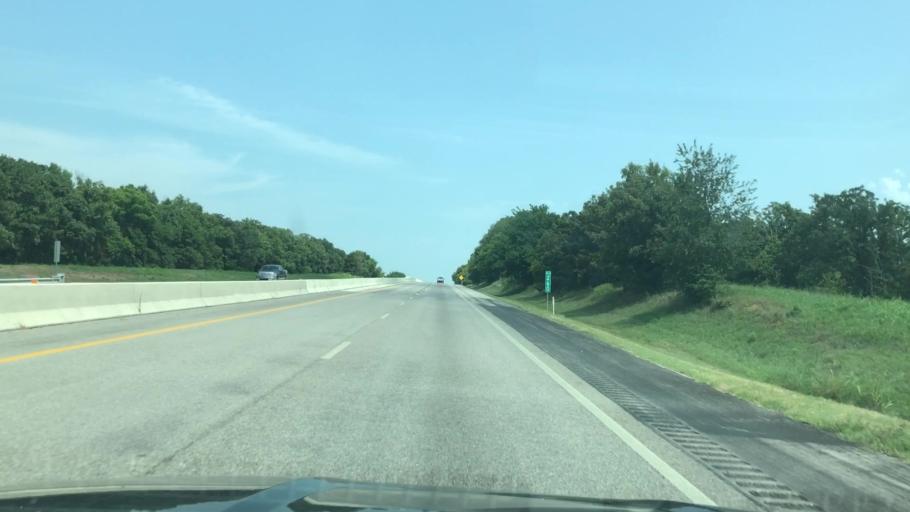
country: US
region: Oklahoma
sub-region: Rogers County
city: Justice
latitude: 36.3403
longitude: -95.4979
